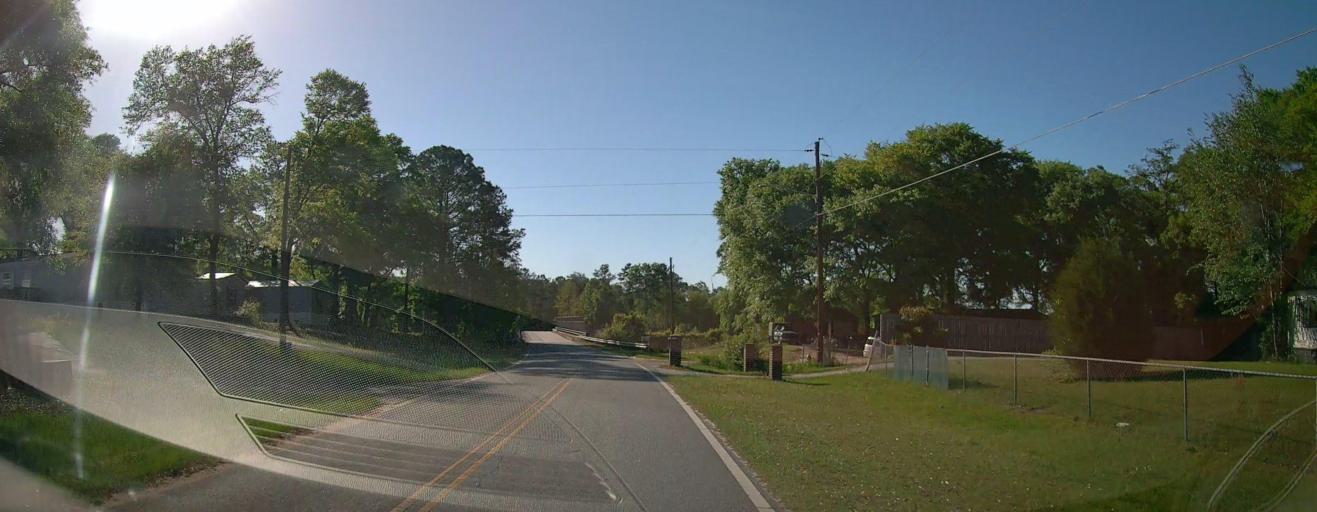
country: US
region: Georgia
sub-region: Houston County
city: Perry
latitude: 32.4545
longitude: -83.7508
